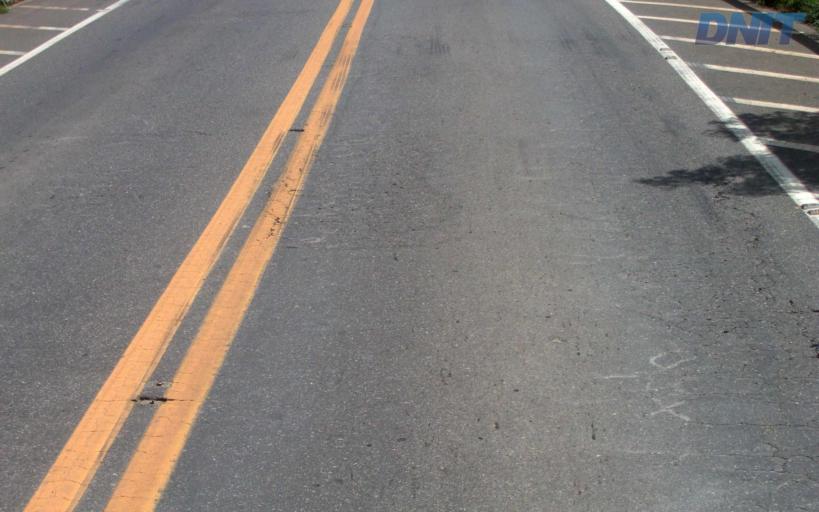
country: BR
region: Minas Gerais
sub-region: Governador Valadares
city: Governador Valadares
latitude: -19.0397
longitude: -42.1484
